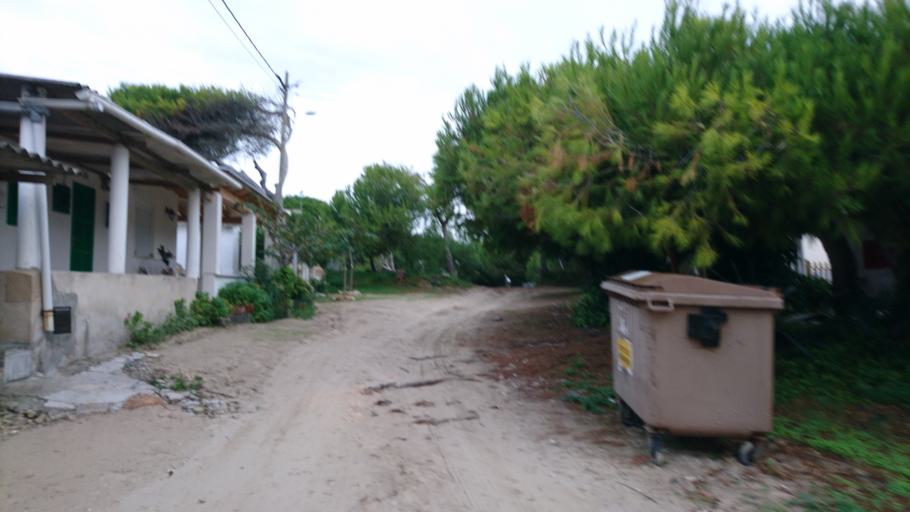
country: ES
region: Balearic Islands
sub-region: Illes Balears
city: Port d'Alcudia
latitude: 39.7740
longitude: 3.1433
